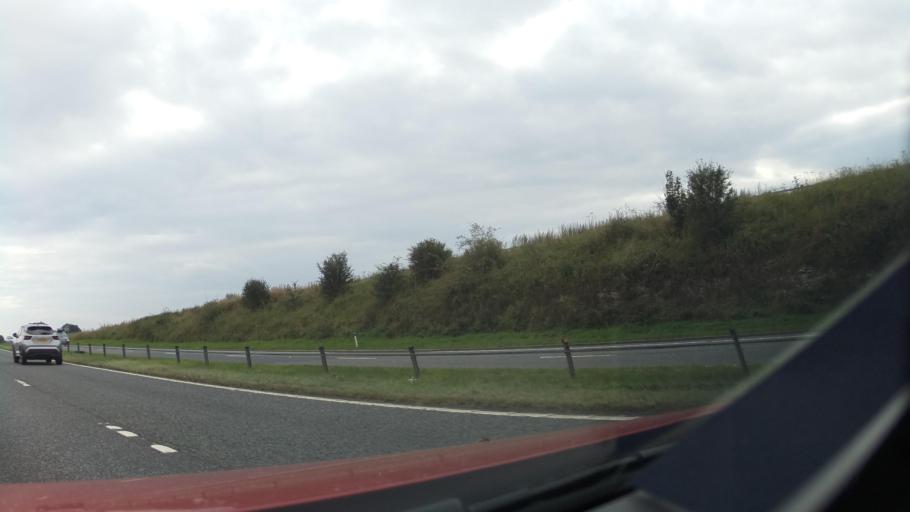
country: GB
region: England
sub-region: County Durham
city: Coxhoe
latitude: 54.6975
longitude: -1.4986
